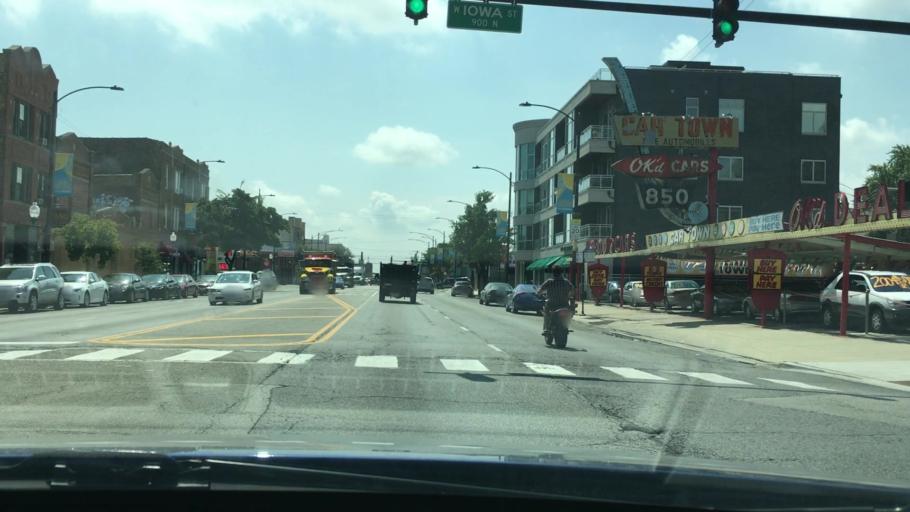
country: US
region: Illinois
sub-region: Cook County
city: Chicago
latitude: 41.8976
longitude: -87.6869
